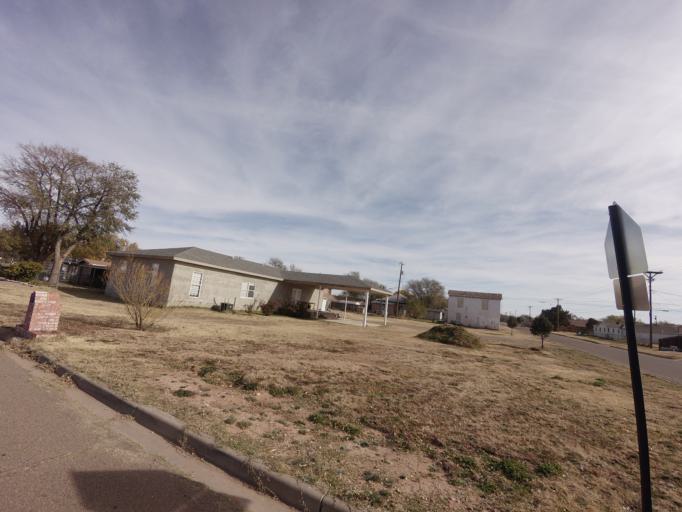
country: US
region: New Mexico
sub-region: Curry County
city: Clovis
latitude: 34.4112
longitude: -103.1914
